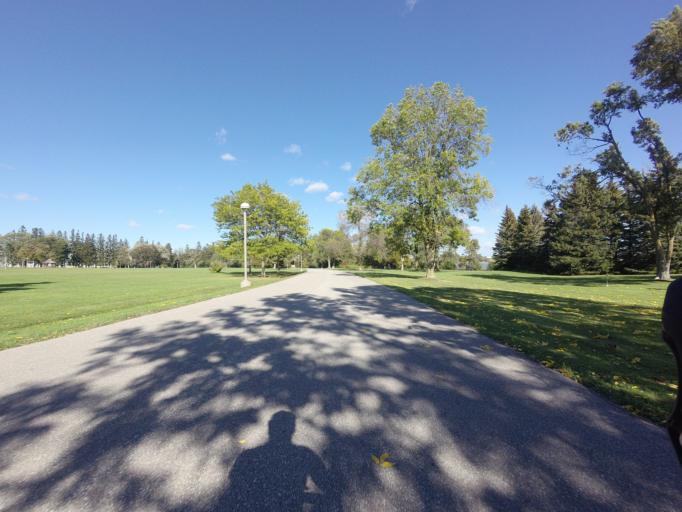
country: CA
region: Ontario
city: Ajax
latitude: 43.8480
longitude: -78.9407
